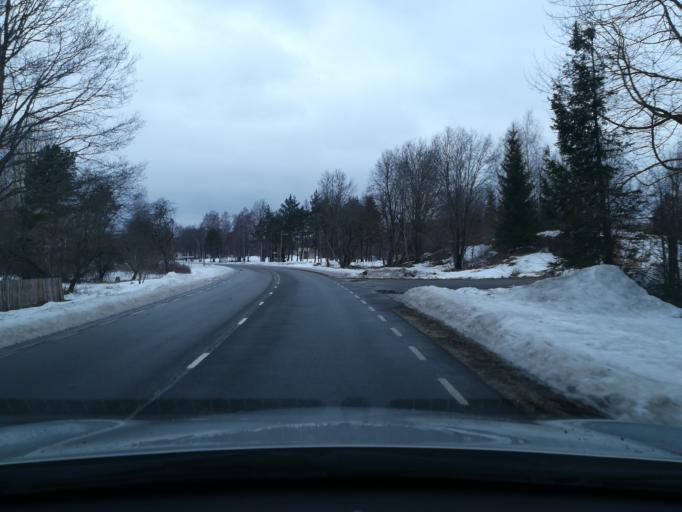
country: EE
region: Harju
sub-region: Nissi vald
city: Turba
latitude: 59.0723
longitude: 24.2483
